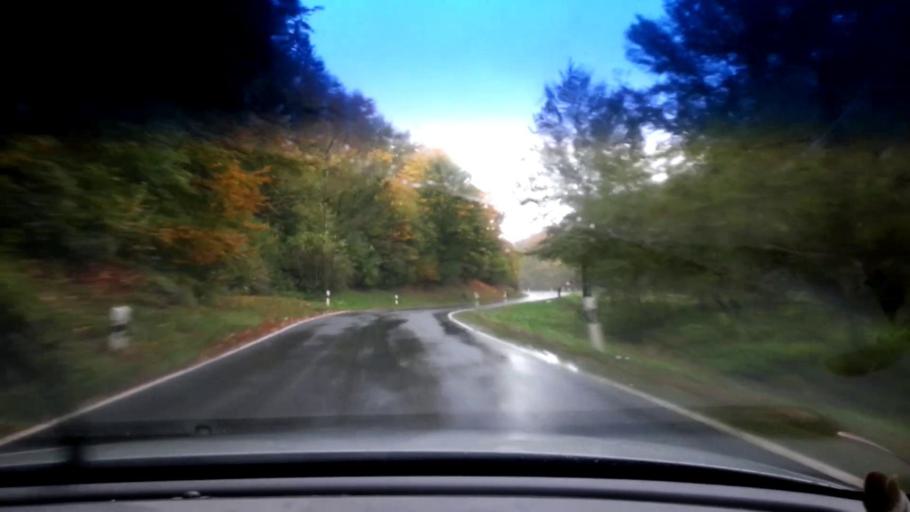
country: DE
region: Bavaria
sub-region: Upper Franconia
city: Stadelhofen
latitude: 50.0328
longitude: 11.2020
